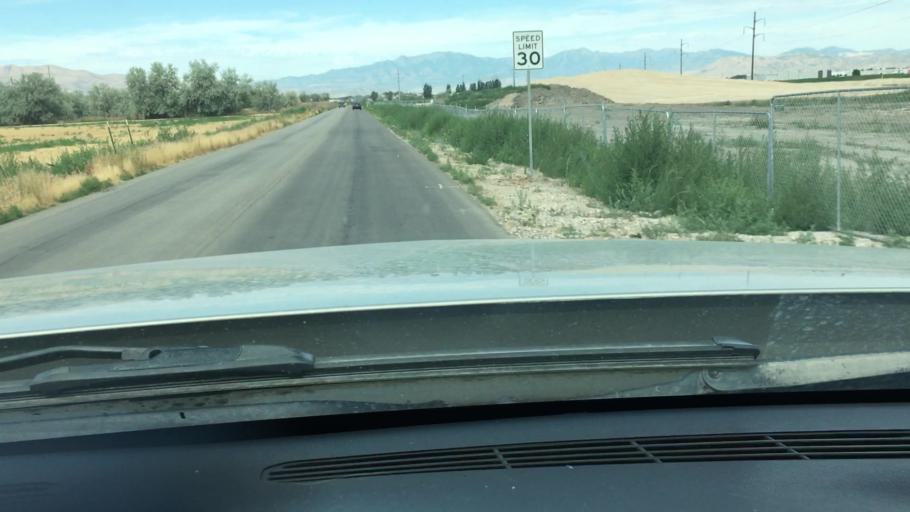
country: US
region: Utah
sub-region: Utah County
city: Pleasant Grove
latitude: 40.3442
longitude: -111.7648
